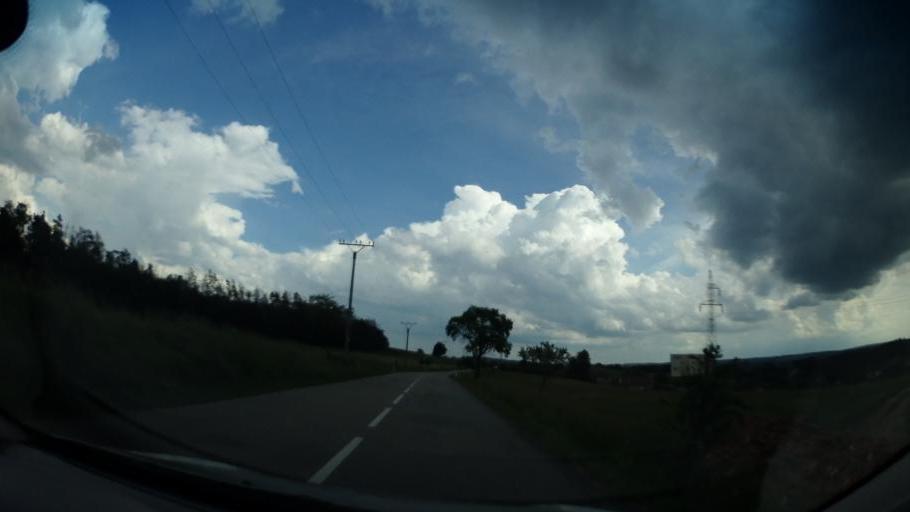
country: CZ
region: South Moravian
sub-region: Okres Brno-Venkov
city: Dolni Loucky
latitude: 49.3980
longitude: 16.3274
